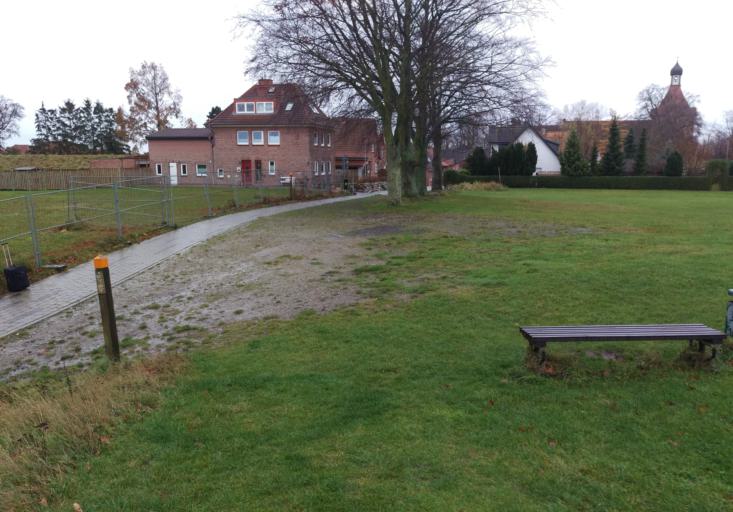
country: DE
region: Schleswig-Holstein
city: Oldenburg in Holstein
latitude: 54.2945
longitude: 10.8854
